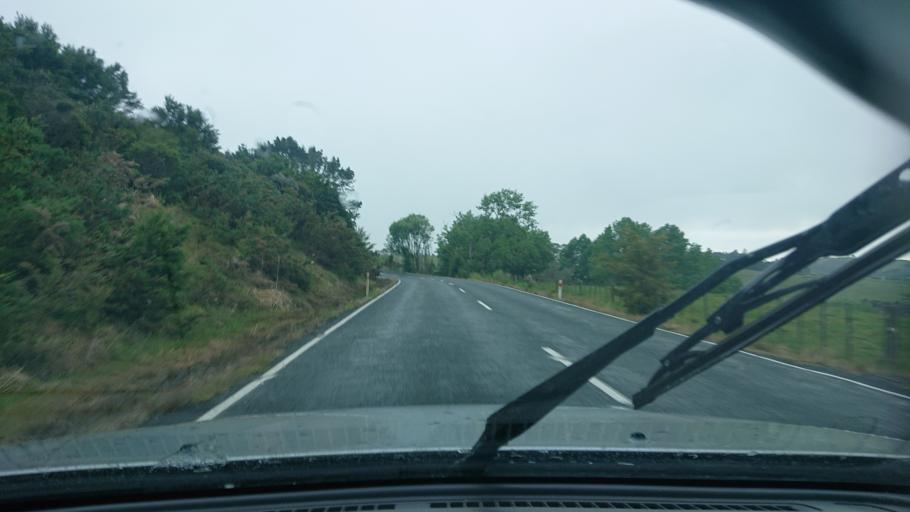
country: NZ
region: Auckland
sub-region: Auckland
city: Wellsford
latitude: -36.3383
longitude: 174.3854
